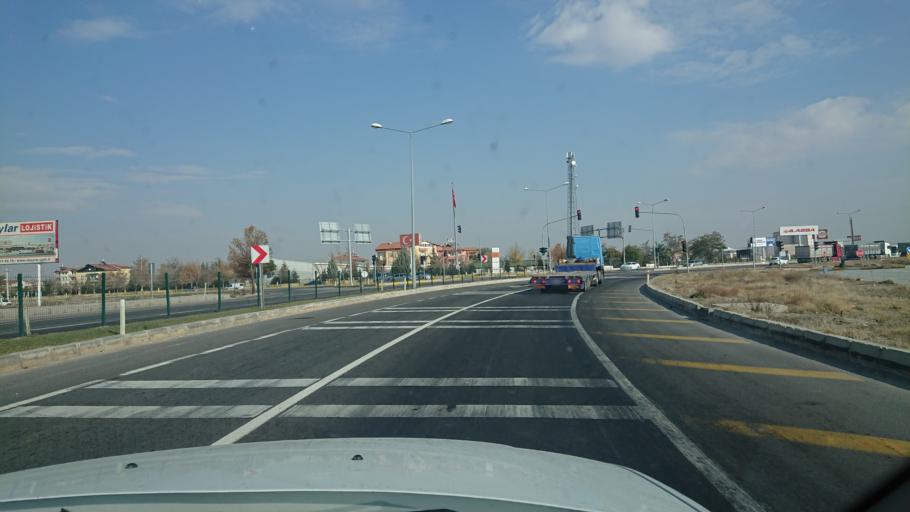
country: TR
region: Aksaray
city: Aksaray
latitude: 38.3557
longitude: 33.9689
